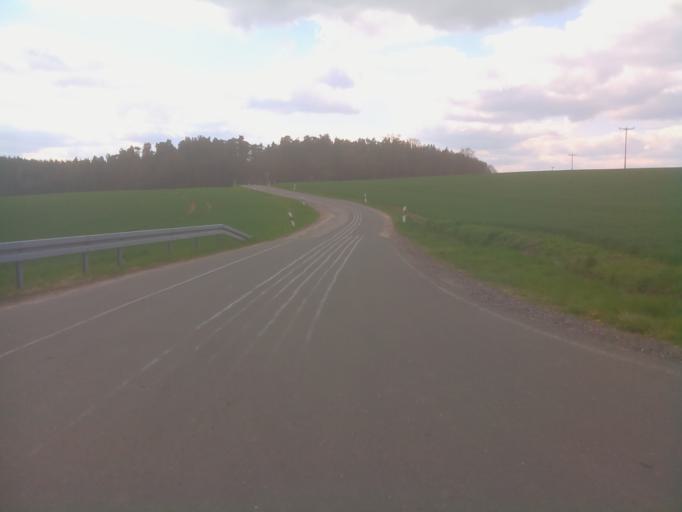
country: DE
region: Thuringia
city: Grossbockedra
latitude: 50.8366
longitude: 11.6669
